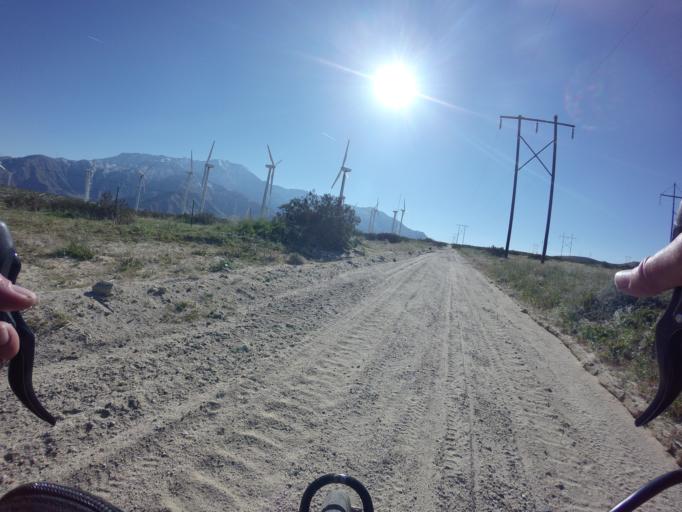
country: US
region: California
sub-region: Riverside County
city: Garnet
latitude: 33.9313
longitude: -116.6263
